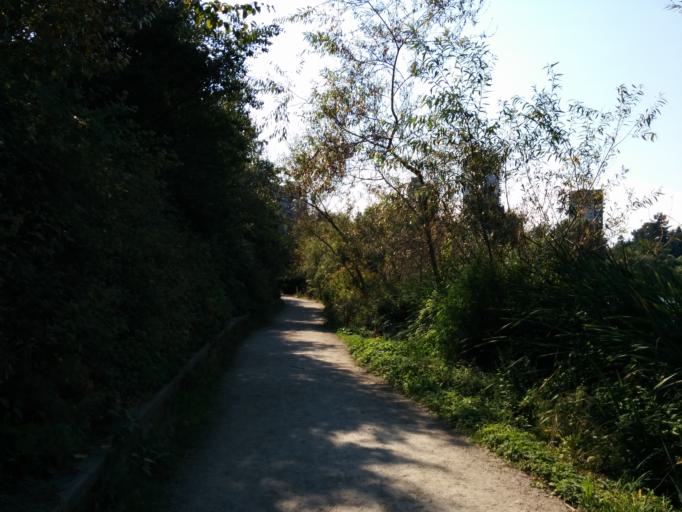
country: CA
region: British Columbia
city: West End
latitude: 49.2955
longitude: -123.1369
